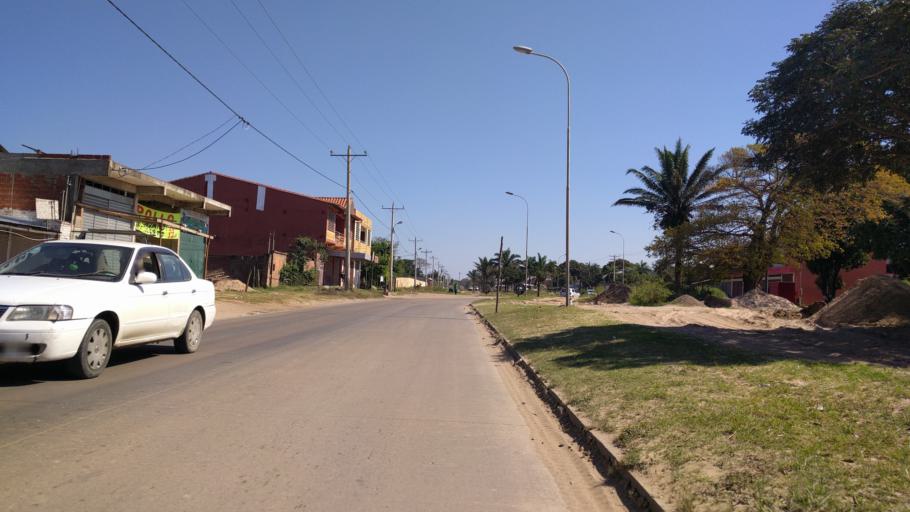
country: BO
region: Santa Cruz
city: Santa Cruz de la Sierra
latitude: -17.8479
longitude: -63.2063
